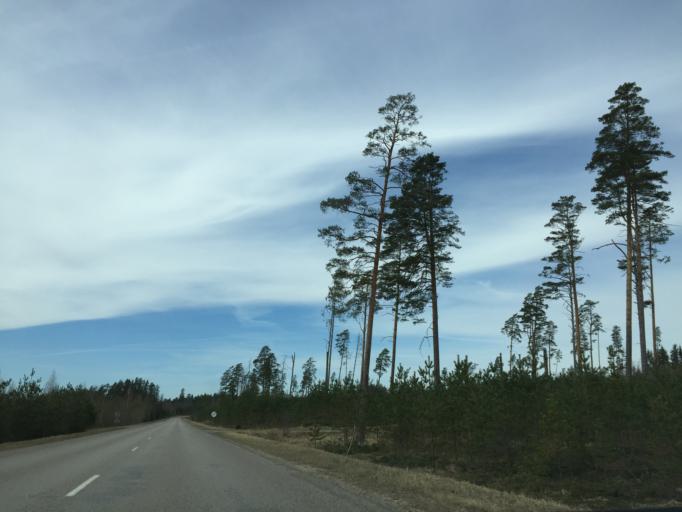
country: LV
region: Valkas Rajons
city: Valka
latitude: 57.8017
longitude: 25.8496
